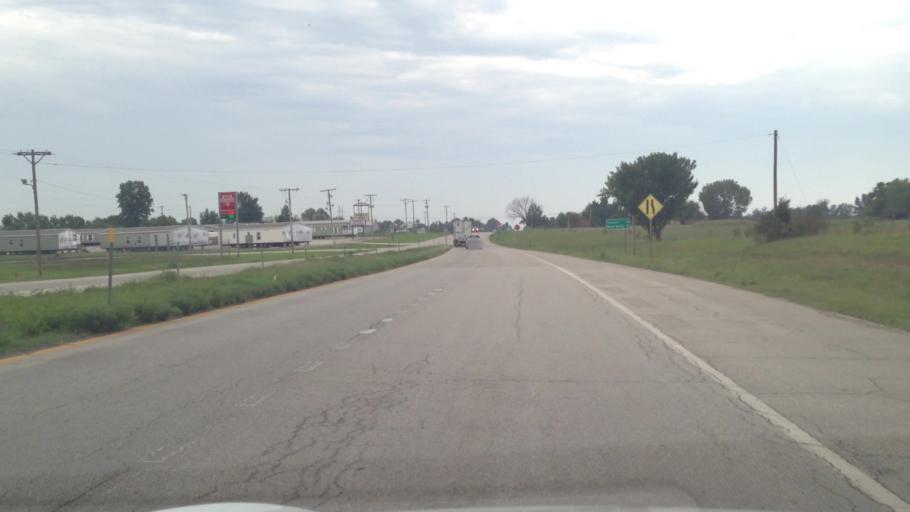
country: US
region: Kansas
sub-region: Crawford County
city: Pittsburg
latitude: 37.3383
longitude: -94.7056
